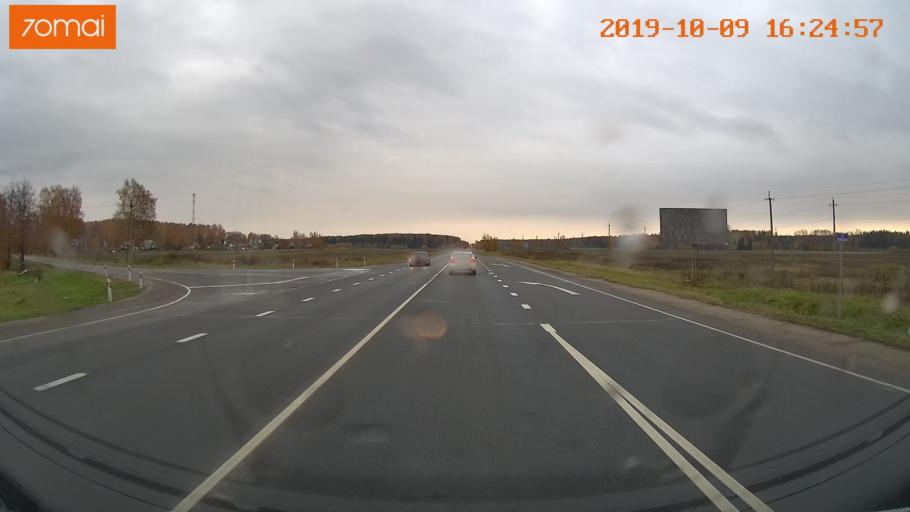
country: RU
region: Kostroma
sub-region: Kostromskoy Rayon
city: Kostroma
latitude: 57.6471
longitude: 40.9153
